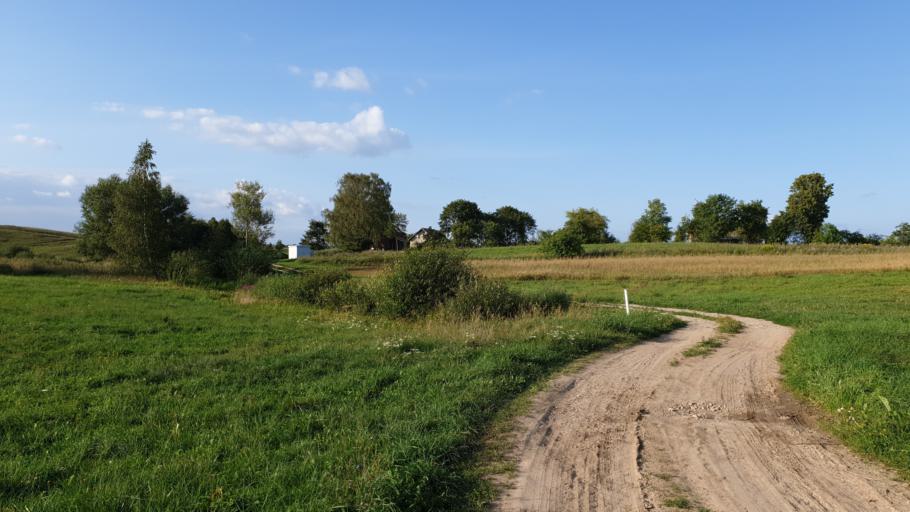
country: LT
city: Grigiskes
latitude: 54.7725
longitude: 25.0323
